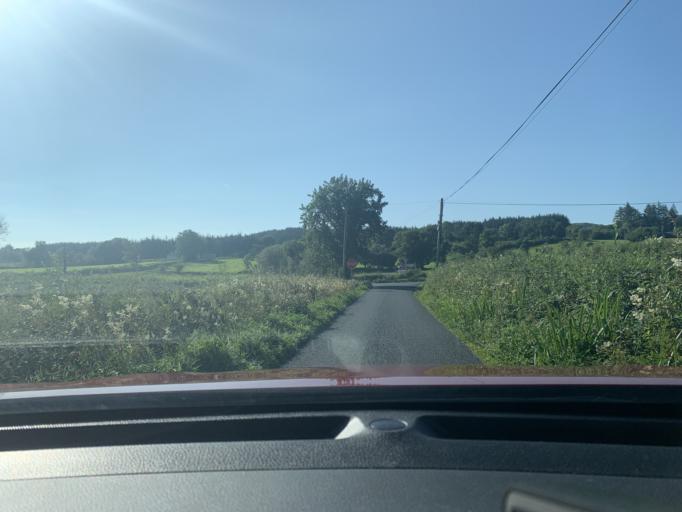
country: IE
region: Connaught
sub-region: Sligo
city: Tobercurry
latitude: 54.0823
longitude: -8.8153
